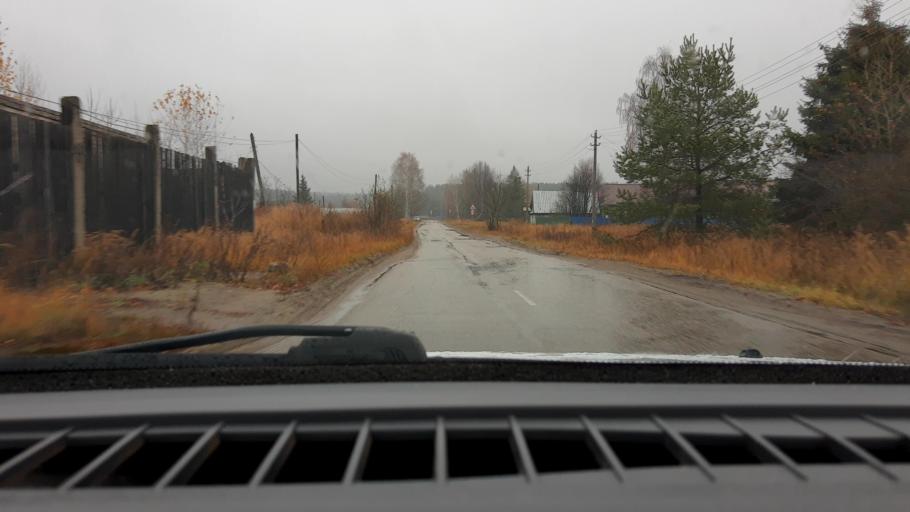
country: RU
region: Nizjnij Novgorod
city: Linda
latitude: 56.6827
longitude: 44.1987
